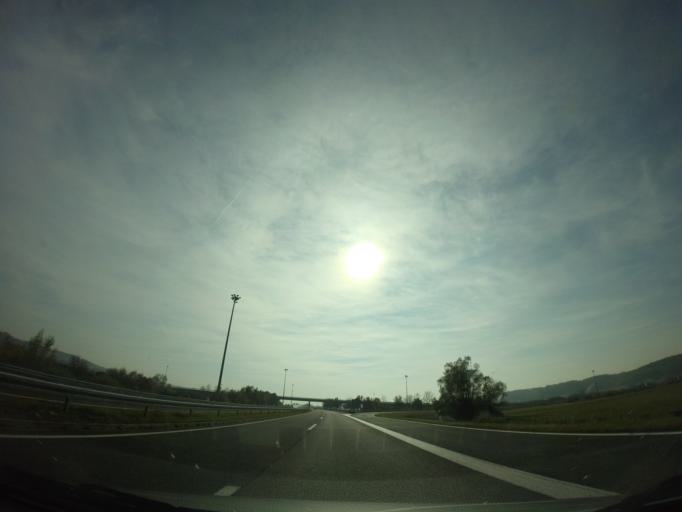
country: HR
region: Zagrebacka
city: Brckovljani
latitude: 45.9952
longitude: 16.2870
